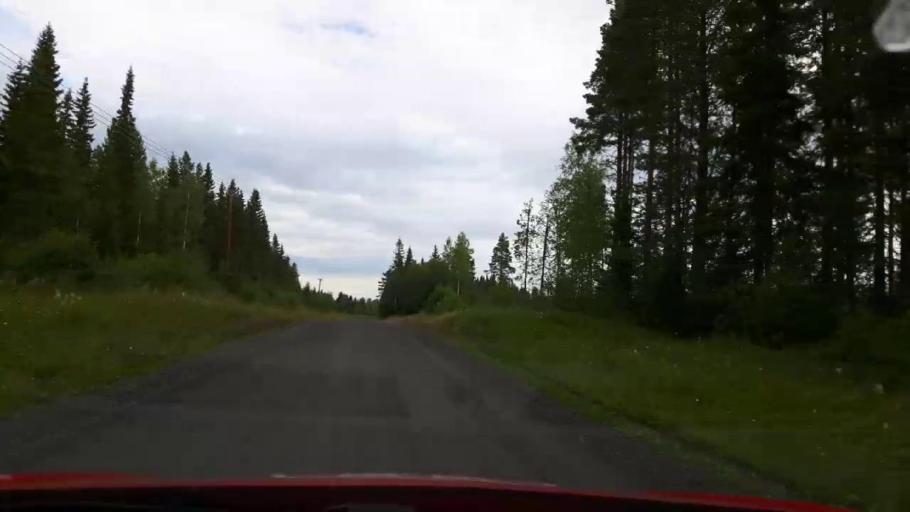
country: SE
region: Jaemtland
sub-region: Stroemsunds Kommun
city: Stroemsund
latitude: 63.5123
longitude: 15.3420
